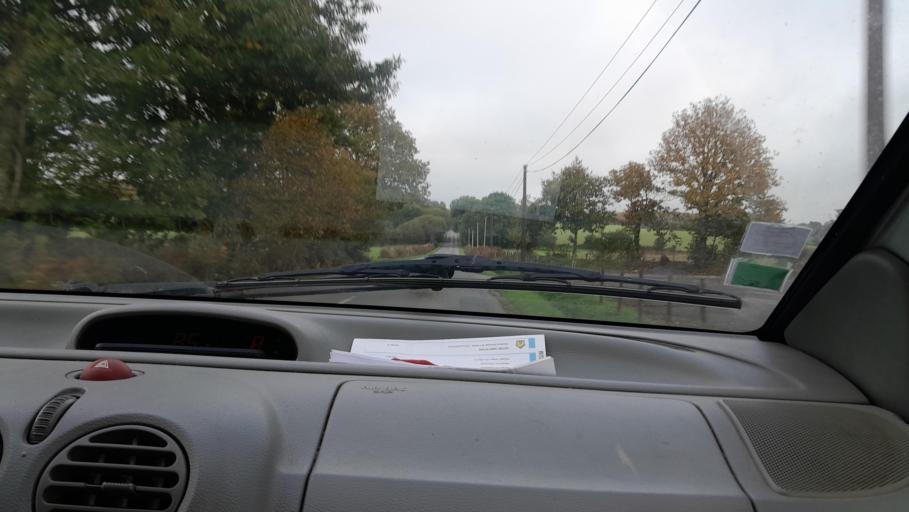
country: FR
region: Pays de la Loire
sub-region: Departement de la Mayenne
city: Juvigne
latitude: 48.2223
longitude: -1.0959
